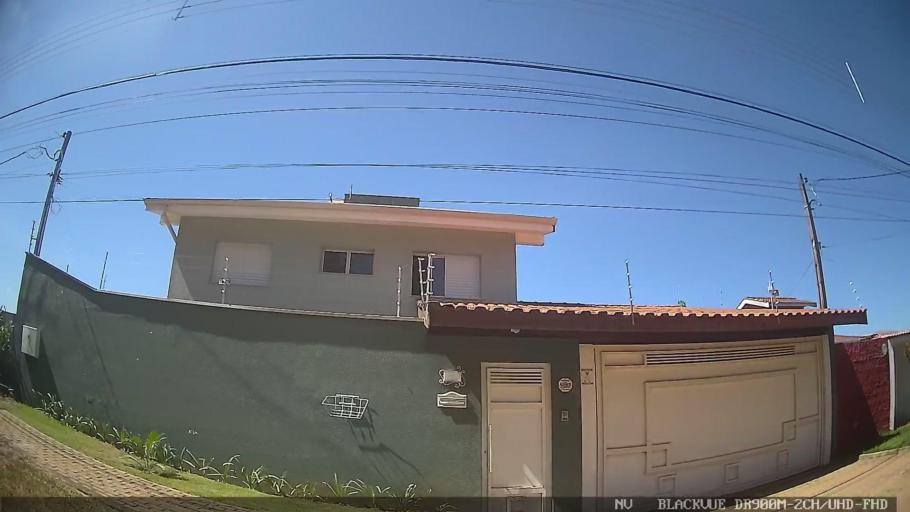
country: BR
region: Sao Paulo
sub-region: Atibaia
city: Atibaia
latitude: -23.1026
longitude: -46.5741
